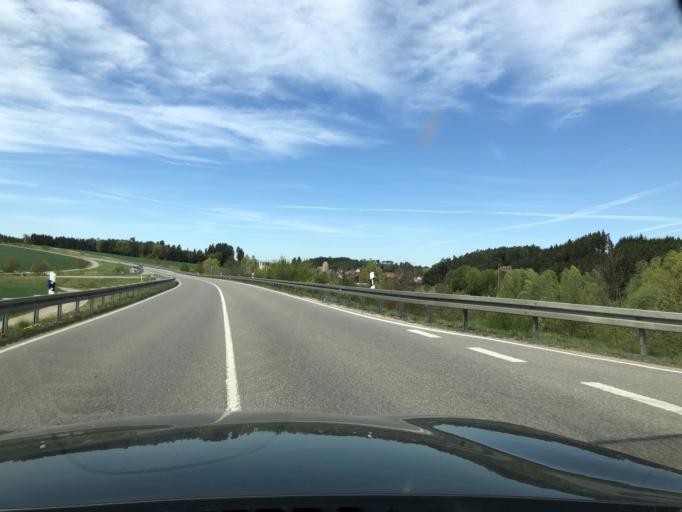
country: DE
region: Bavaria
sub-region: Swabia
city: Laugna
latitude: 48.5455
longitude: 10.7258
